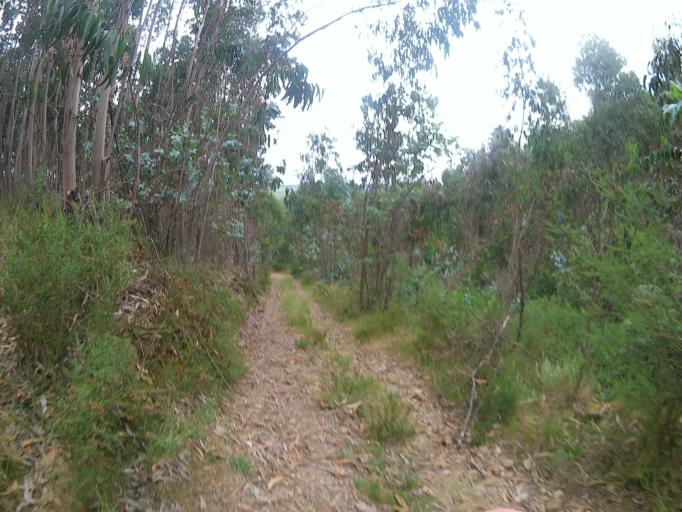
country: PT
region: Aveiro
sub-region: Albergaria-A-Velha
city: Branca
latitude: 40.7655
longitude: -8.4311
